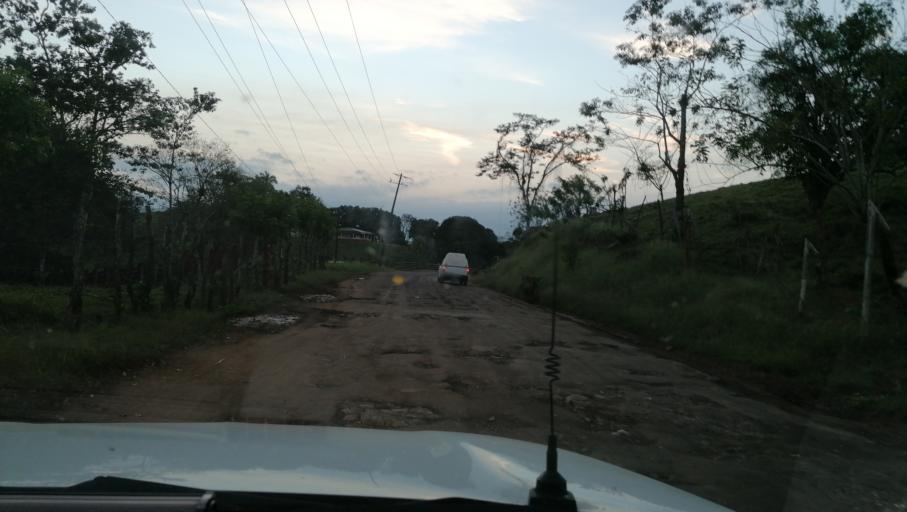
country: MX
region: Chiapas
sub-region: Ostuacan
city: Nuevo Juan del Grijalva
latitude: 17.4466
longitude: -93.3573
